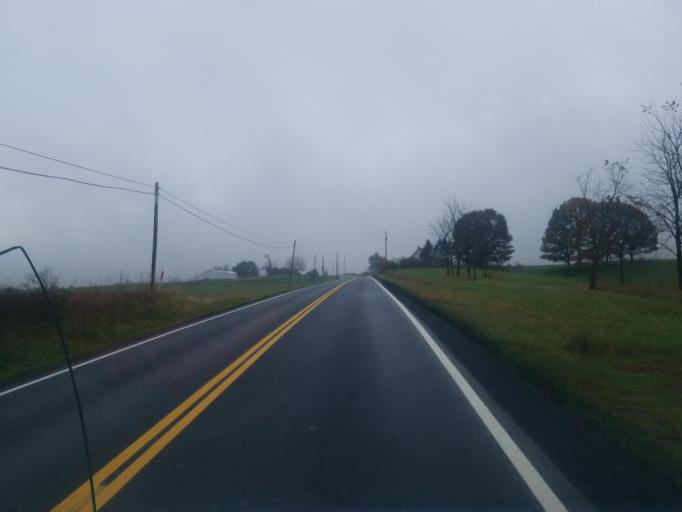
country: US
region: Ohio
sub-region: Morgan County
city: McConnelsville
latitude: 39.5594
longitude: -81.8296
